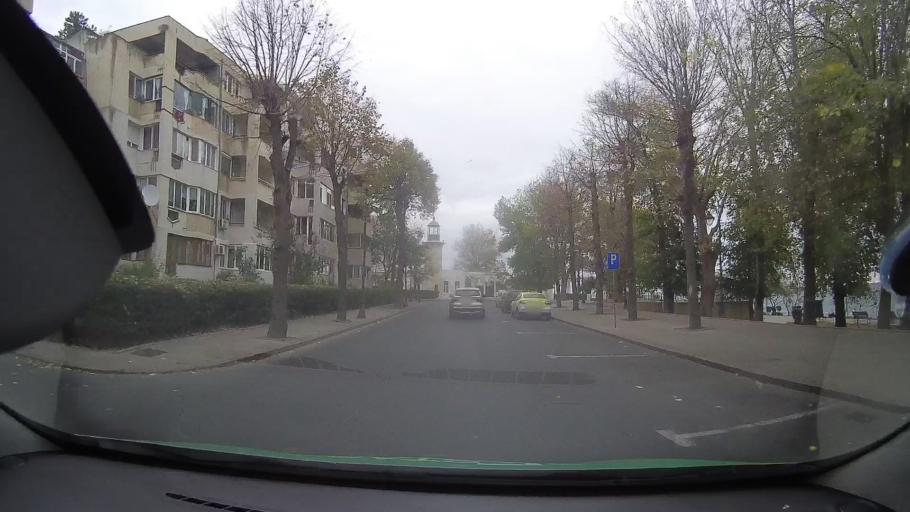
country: RO
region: Constanta
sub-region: Municipiul Constanta
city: Constanta
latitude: 44.1715
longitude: 28.6638
